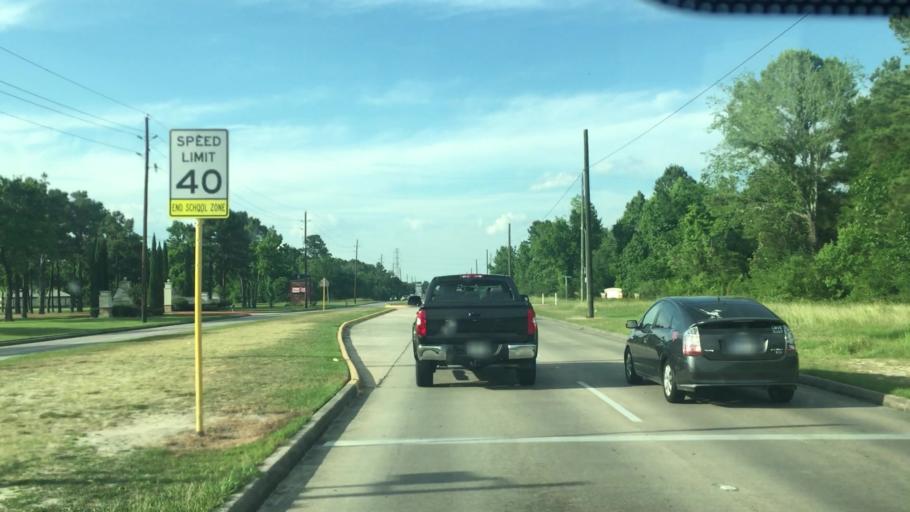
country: US
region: Texas
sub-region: Harris County
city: Hudson
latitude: 29.9668
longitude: -95.4967
